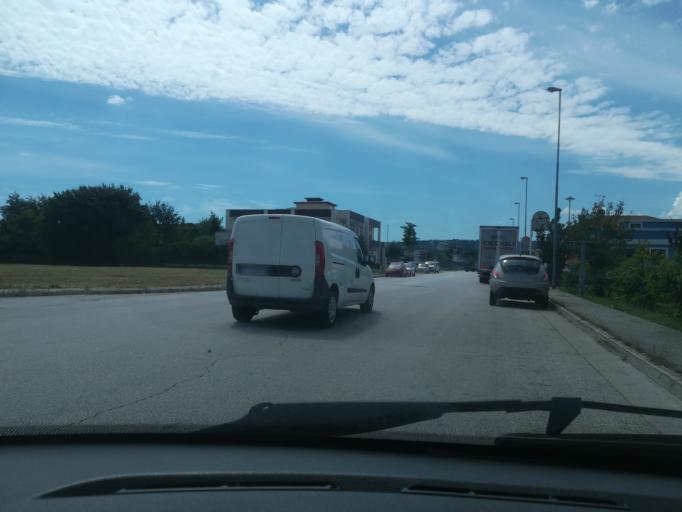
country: IT
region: The Marches
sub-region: Provincia di Macerata
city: Santa Maria Apparente
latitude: 43.2859
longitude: 13.6824
